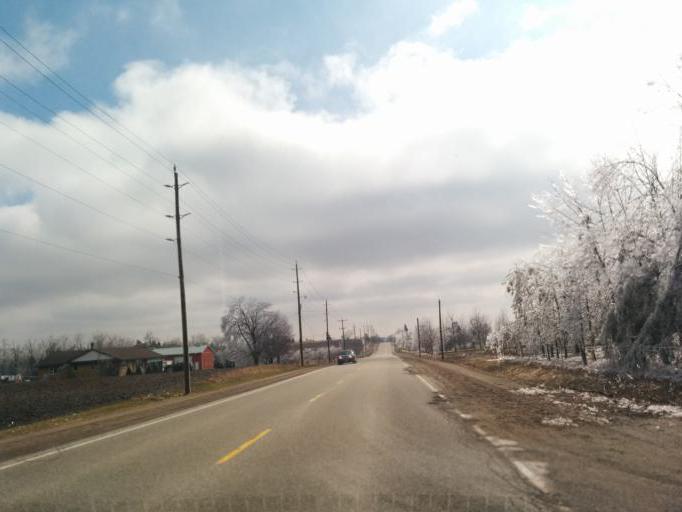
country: CA
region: Ontario
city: Waterloo
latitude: 43.6394
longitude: -80.5488
